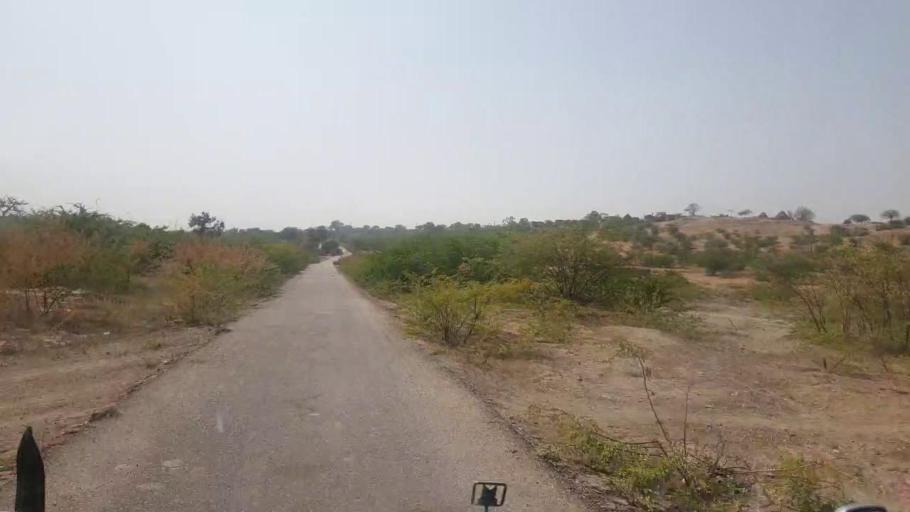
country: PK
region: Sindh
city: Islamkot
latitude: 25.1265
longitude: 70.2192
